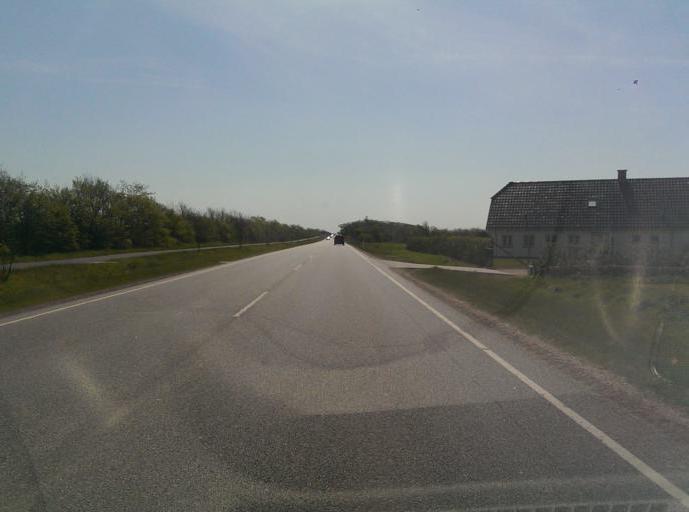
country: DK
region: South Denmark
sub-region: Esbjerg Kommune
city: Ribe
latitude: 55.3760
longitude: 8.7606
